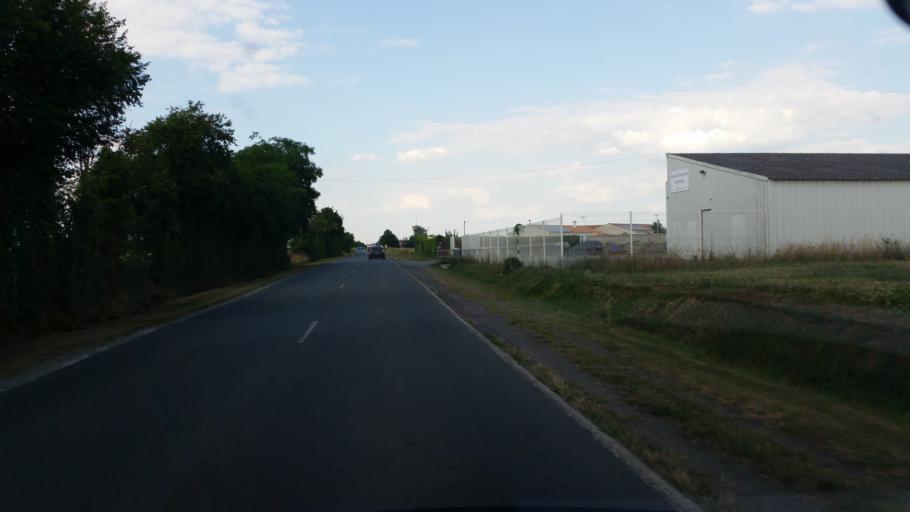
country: FR
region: Poitou-Charentes
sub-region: Departement de la Charente-Maritime
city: Andilly
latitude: 46.2567
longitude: -1.0196
